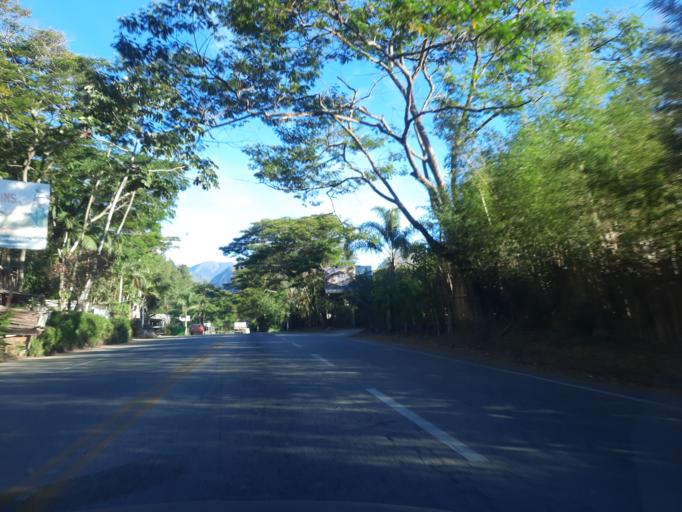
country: BR
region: Rio de Janeiro
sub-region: Petropolis
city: Petropolis
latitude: -22.4101
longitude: -43.1447
